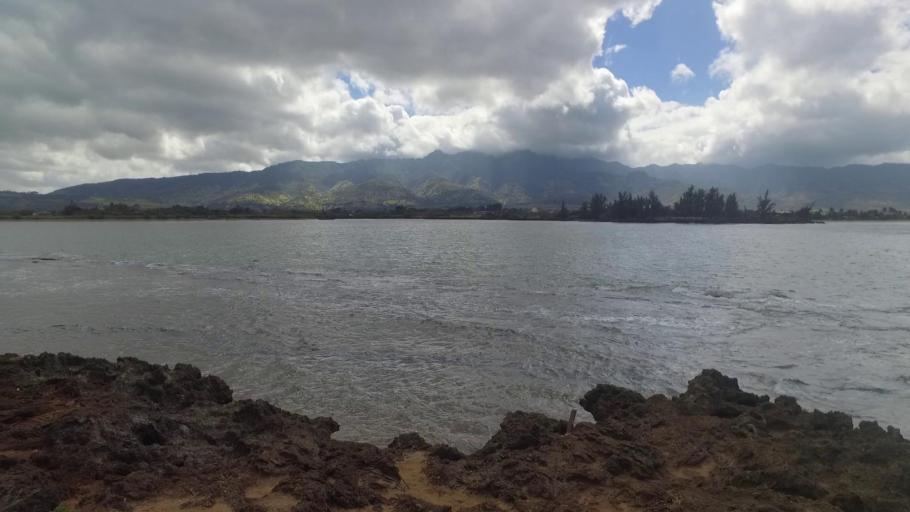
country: US
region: Hawaii
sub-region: Honolulu County
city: Hale'iwa
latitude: 21.5877
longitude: -158.1193
